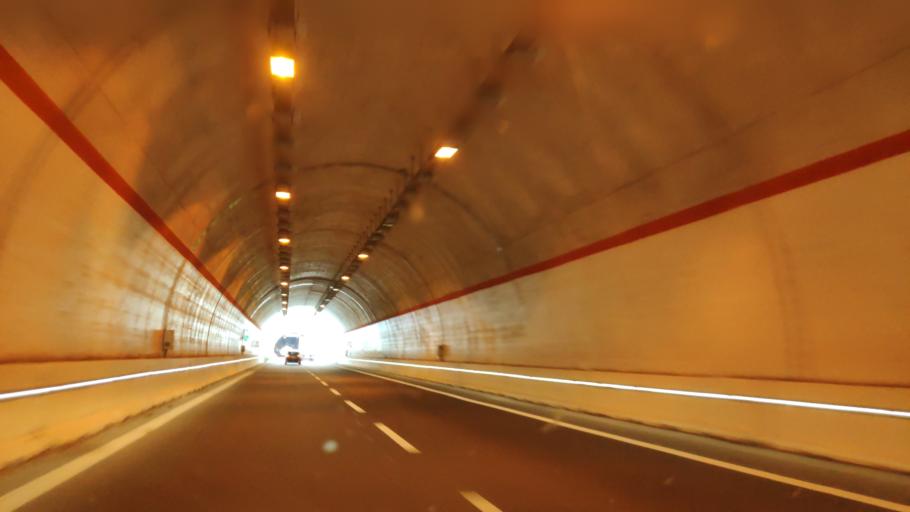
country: IT
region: Calabria
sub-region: Provincia di Reggio Calabria
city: Marina di Gioiosa Ionica
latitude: 38.3139
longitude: 16.3235
